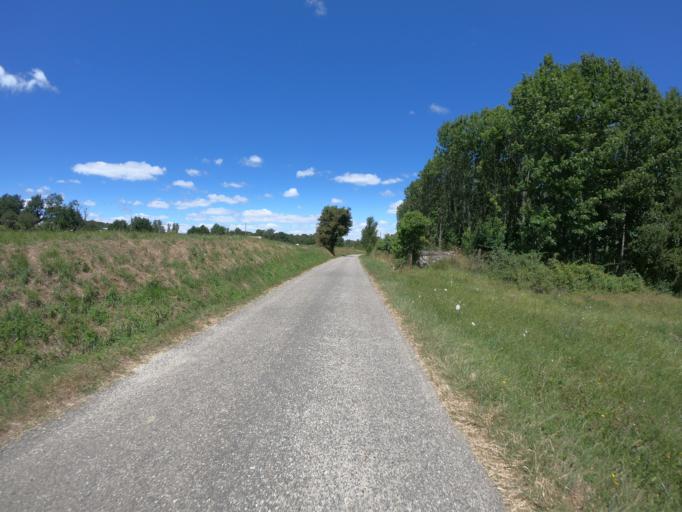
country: FR
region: Midi-Pyrenees
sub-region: Departement de l'Ariege
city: Verniolle
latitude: 43.0802
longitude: 1.7171
